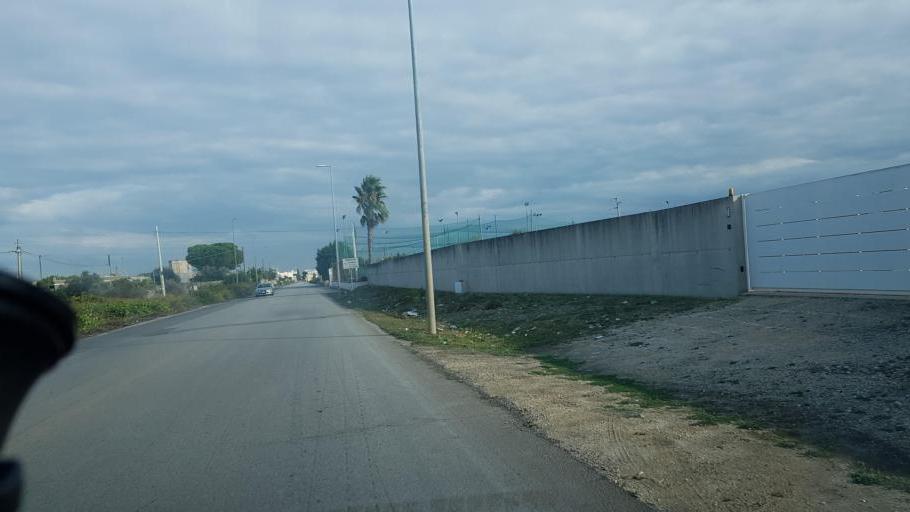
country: IT
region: Apulia
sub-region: Provincia di Brindisi
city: Francavilla Fontana
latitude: 40.5316
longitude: 17.5639
